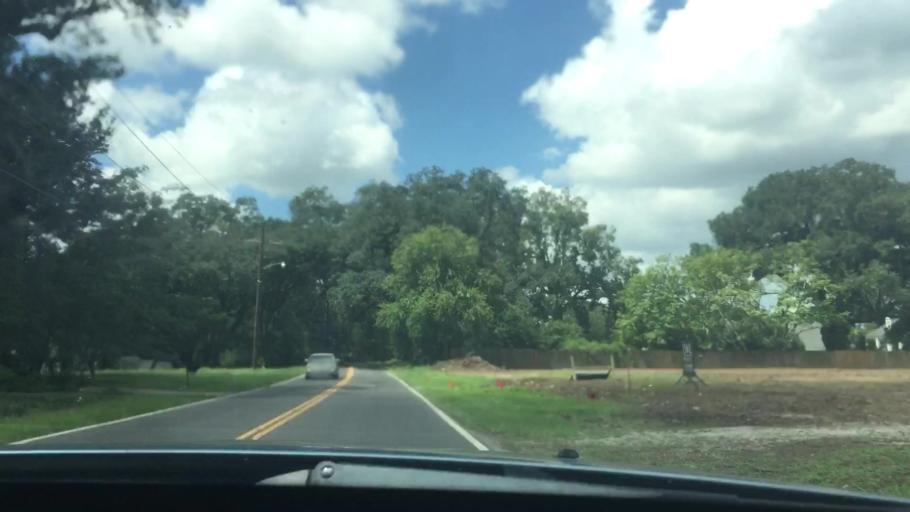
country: US
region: Louisiana
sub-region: East Baton Rouge Parish
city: Gardere
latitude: 30.3728
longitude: -91.1305
